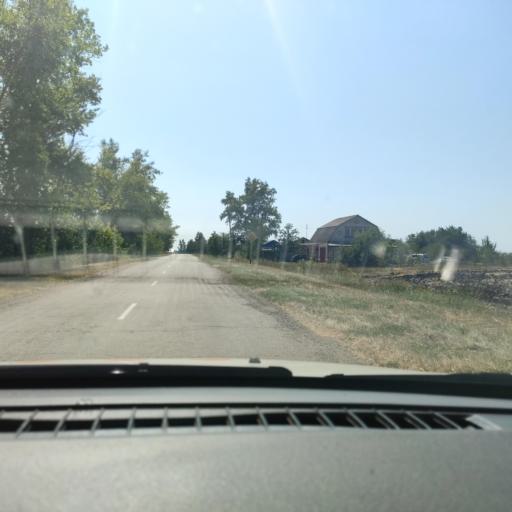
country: RU
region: Voronezj
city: Ostrogozhsk
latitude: 50.7096
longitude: 39.3361
